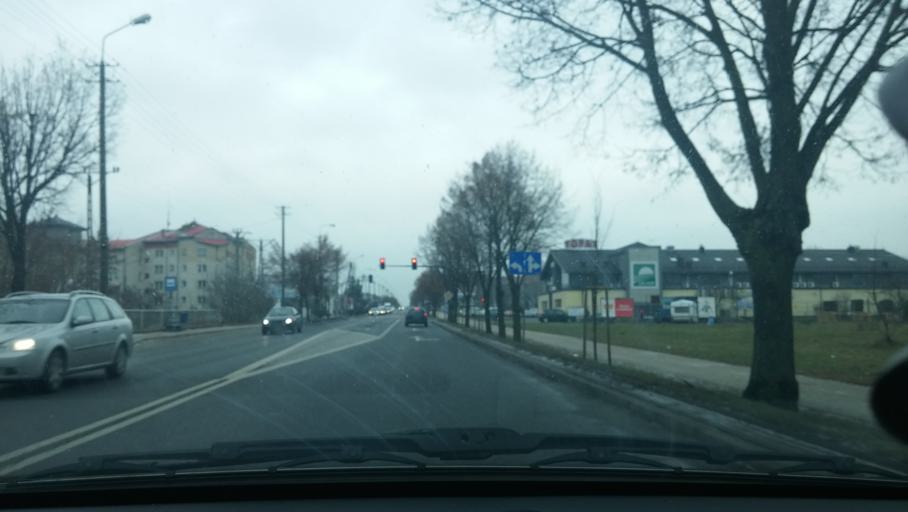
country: PL
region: Masovian Voivodeship
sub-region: Siedlce
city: Siedlce
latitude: 52.1702
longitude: 22.2311
